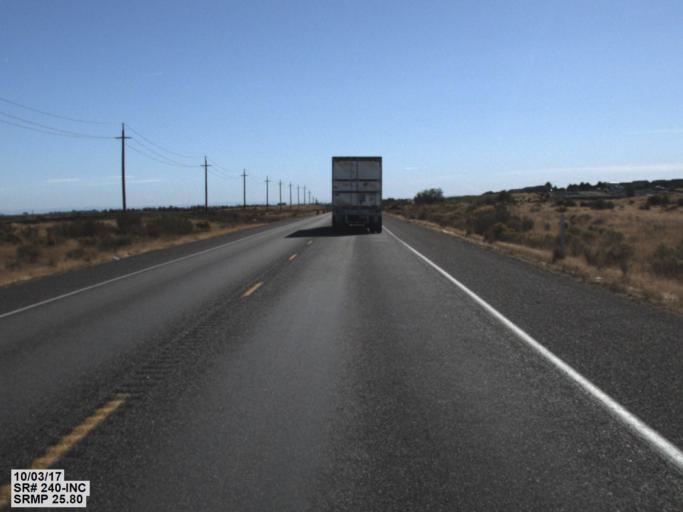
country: US
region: Washington
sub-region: Benton County
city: West Richland
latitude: 46.3355
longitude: -119.3352
